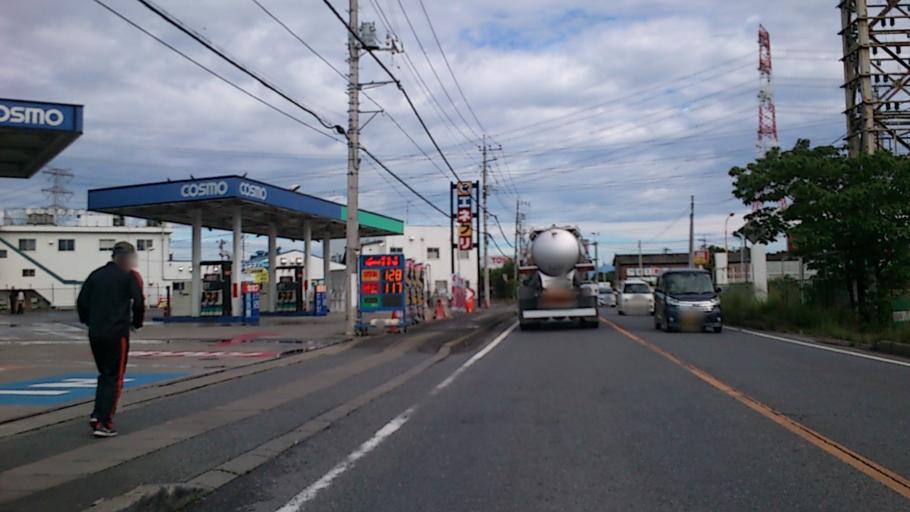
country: JP
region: Saitama
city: Honjo
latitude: 36.2242
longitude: 139.2244
